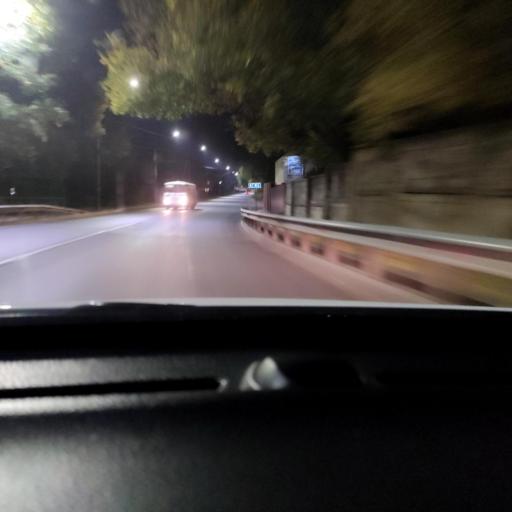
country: RU
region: Voronezj
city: Voronezh
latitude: 51.7284
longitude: 39.2600
